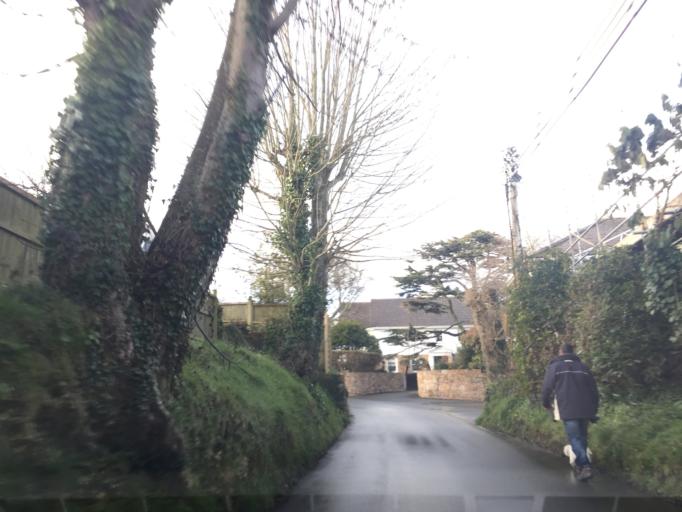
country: JE
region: St Helier
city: Saint Helier
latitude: 49.2035
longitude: -2.1376
